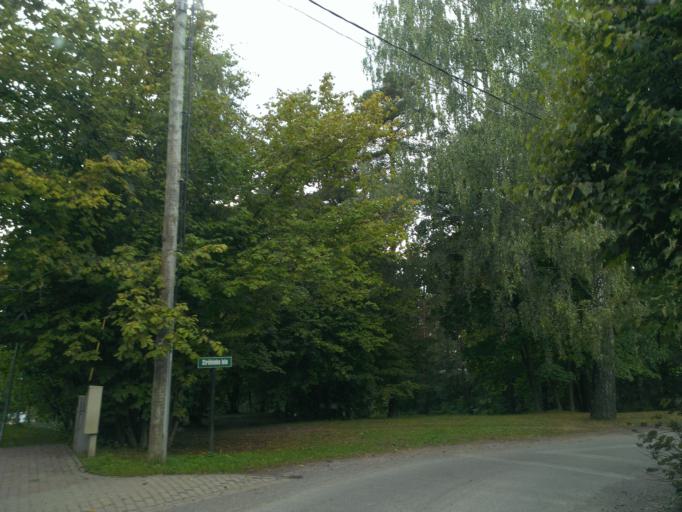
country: LV
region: Ikskile
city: Ikskile
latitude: 56.8352
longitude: 24.4932
